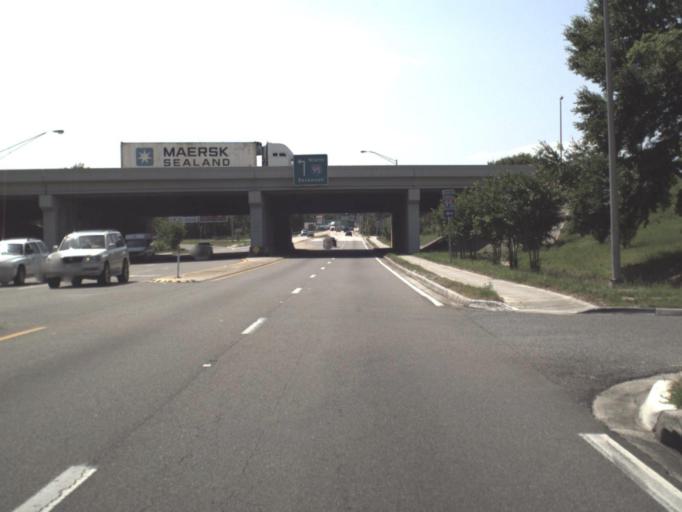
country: US
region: Florida
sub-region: Duval County
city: Jacksonville
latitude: 30.3833
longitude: -81.6735
